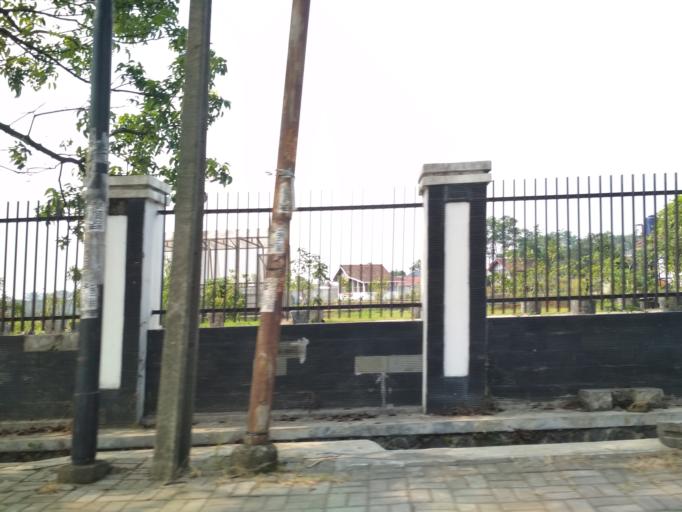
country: ID
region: West Java
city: Bogor
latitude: -6.5786
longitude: 106.7597
